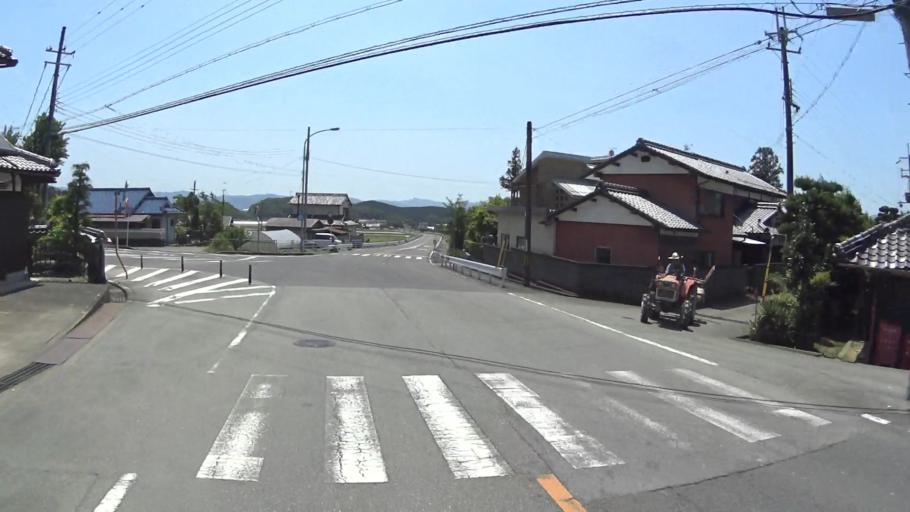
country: JP
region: Kyoto
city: Kameoka
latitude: 35.0839
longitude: 135.5647
